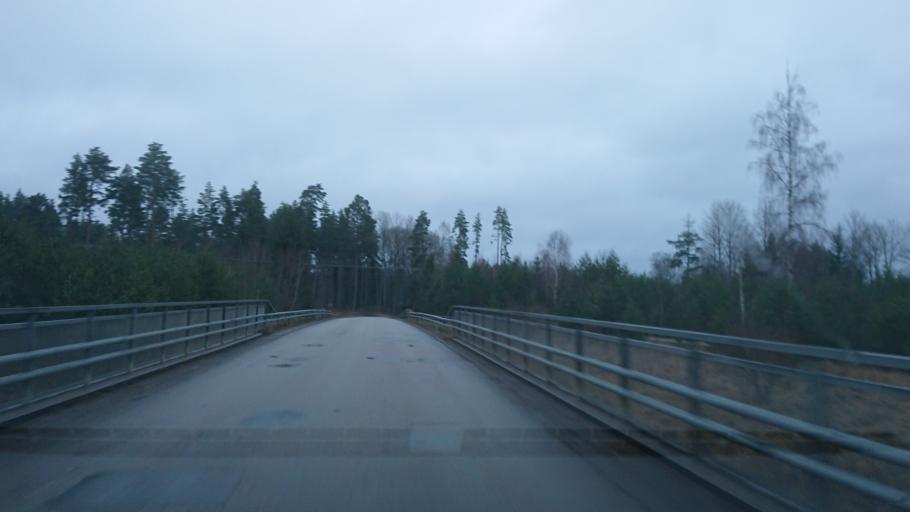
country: SE
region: Uppsala
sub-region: Osthammars Kommun
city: Bjorklinge
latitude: 60.0181
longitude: 17.5828
